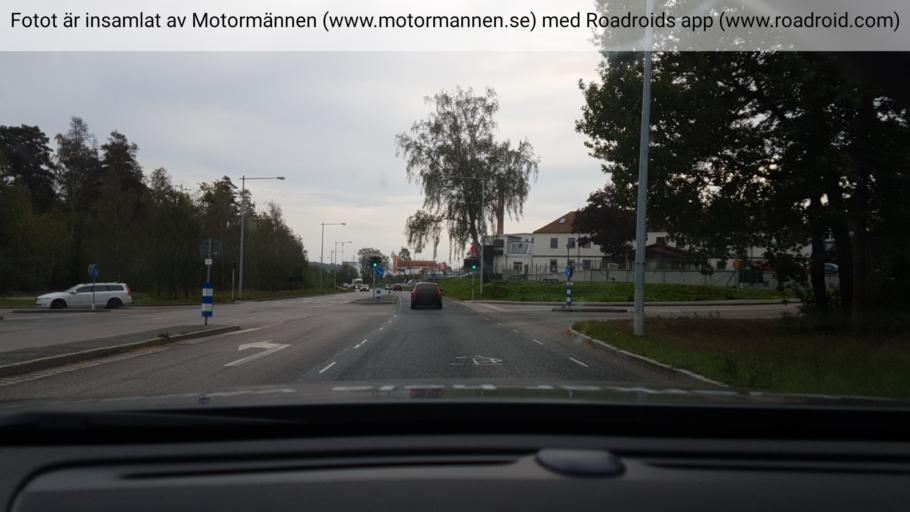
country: SE
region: Stockholm
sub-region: Nynashamns Kommun
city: Nynashamn
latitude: 58.9152
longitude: 17.9564
